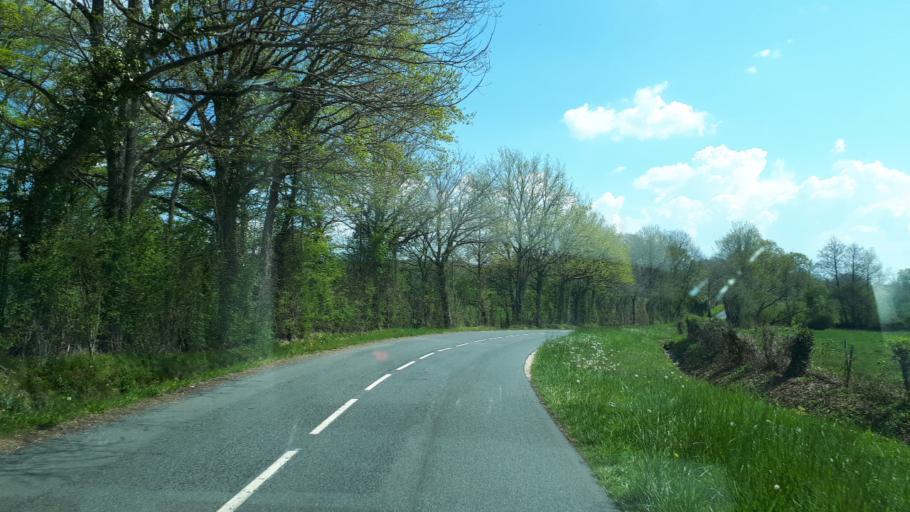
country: FR
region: Centre
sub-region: Departement du Cher
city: Henrichemont
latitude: 47.3051
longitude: 2.6480
